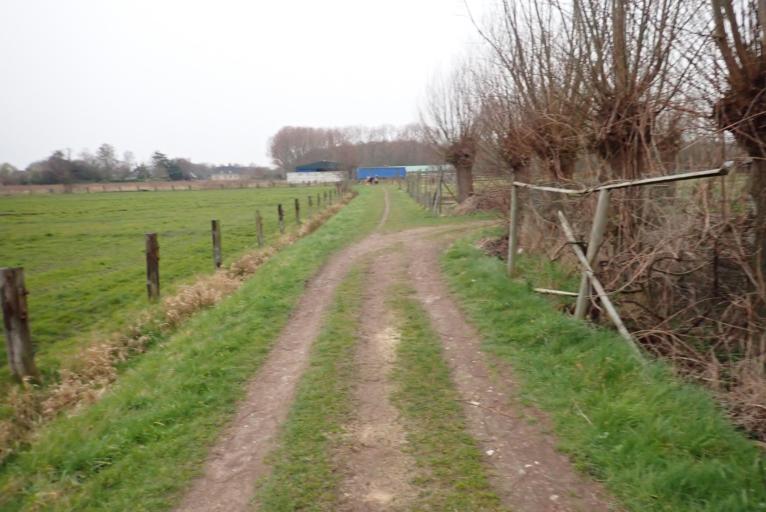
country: BE
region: Flanders
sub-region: Provincie Antwerpen
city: Wijnegem
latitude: 51.2160
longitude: 4.5167
